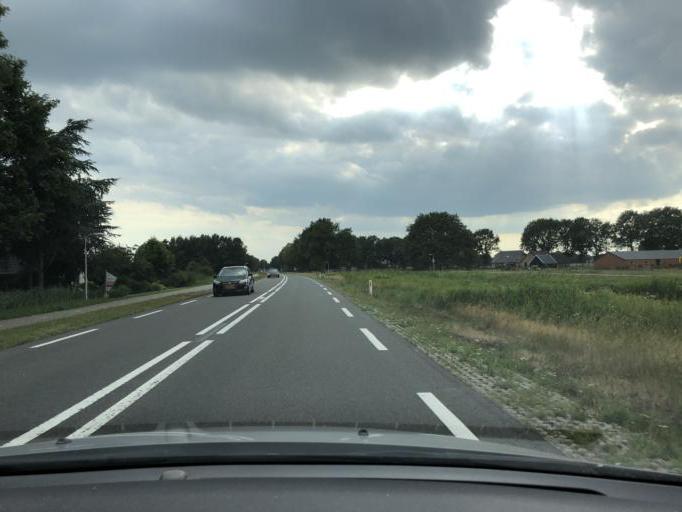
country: NL
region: Overijssel
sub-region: Gemeente Hardenberg
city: Hardenberg
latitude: 52.6322
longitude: 6.5717
